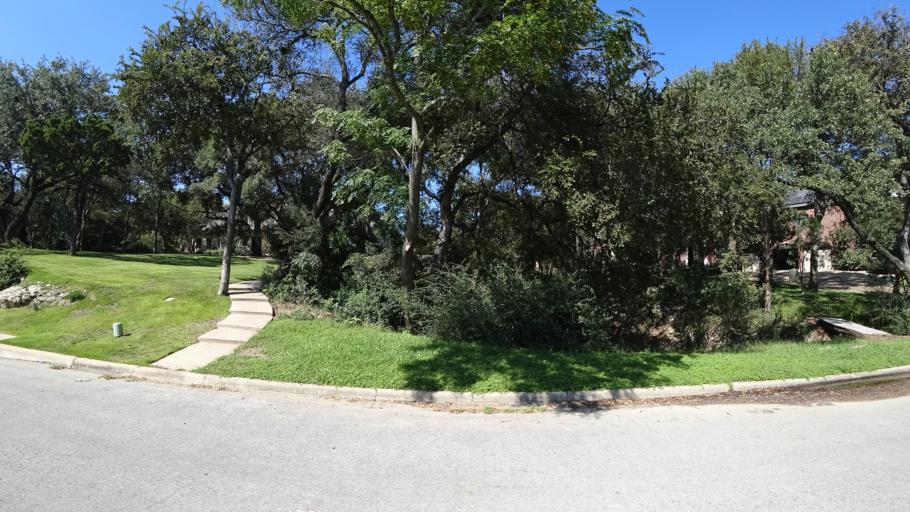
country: US
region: Texas
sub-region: Travis County
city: Rollingwood
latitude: 30.2830
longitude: -97.7921
